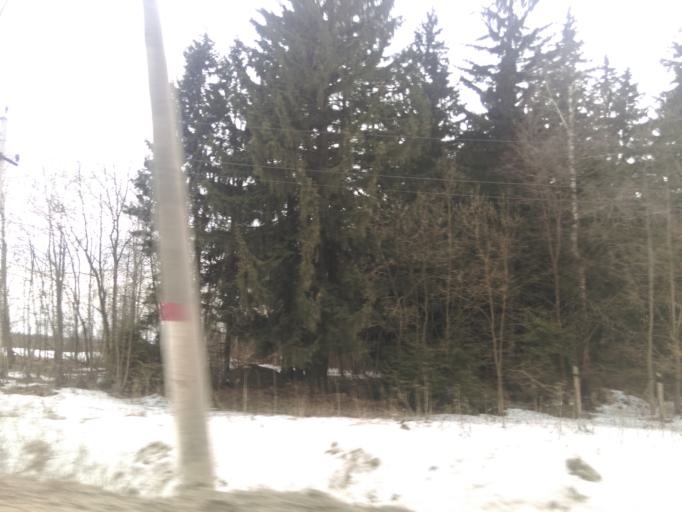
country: RU
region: Moskovskaya
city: Tuchkovo
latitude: 55.6022
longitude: 36.4461
